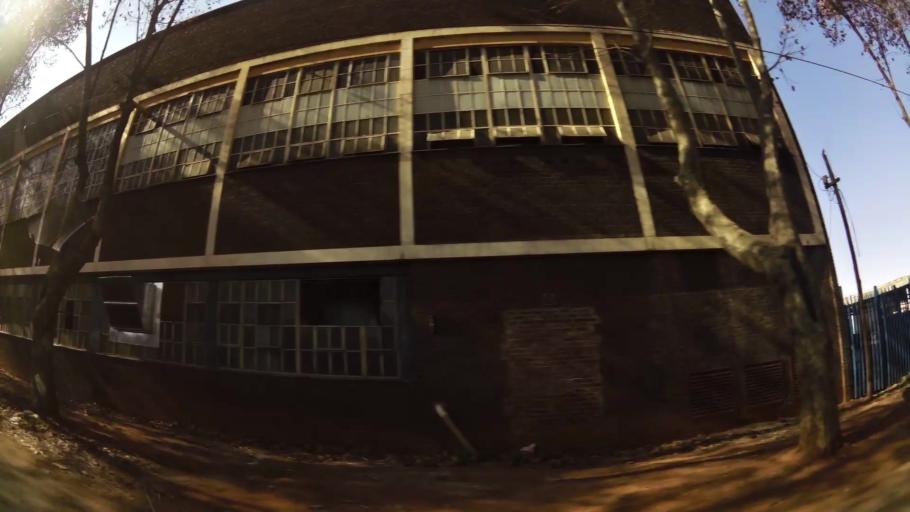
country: ZA
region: Gauteng
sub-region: City of Johannesburg Metropolitan Municipality
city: Johannesburg
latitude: -26.2008
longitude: 27.9775
